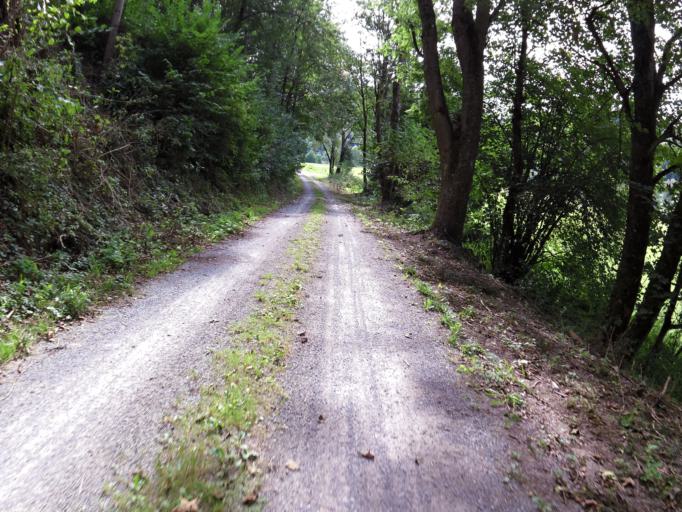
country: DE
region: Baden-Wuerttemberg
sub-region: Freiburg Region
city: Sulz am Neckar
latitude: 48.3505
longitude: 8.5944
